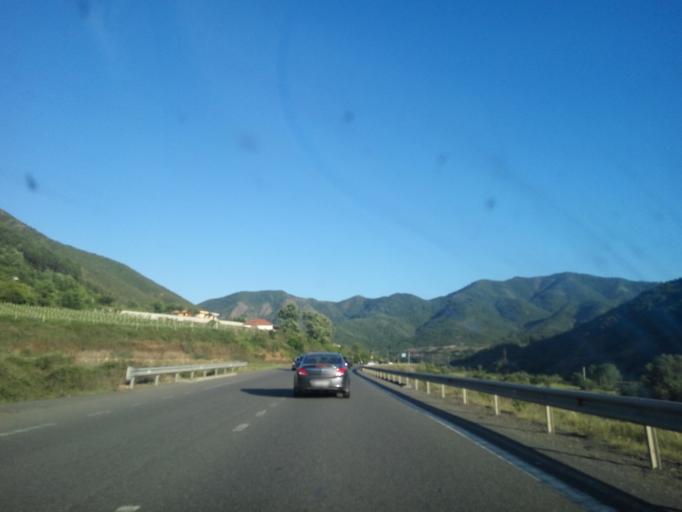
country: AL
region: Lezhe
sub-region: Rrethi i Mirdites
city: Rubik
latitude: 41.7902
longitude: 19.8164
